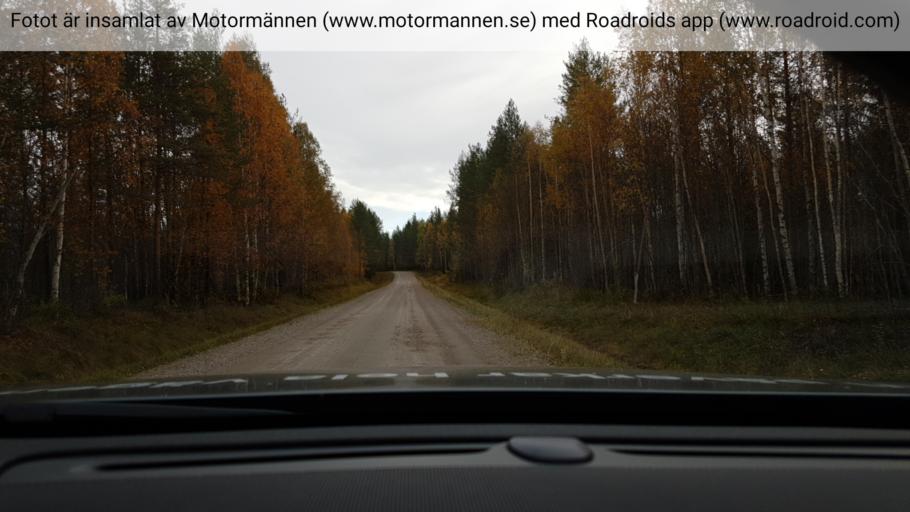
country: SE
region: Norrbotten
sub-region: Overkalix Kommun
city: OEverkalix
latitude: 66.2929
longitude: 22.9512
